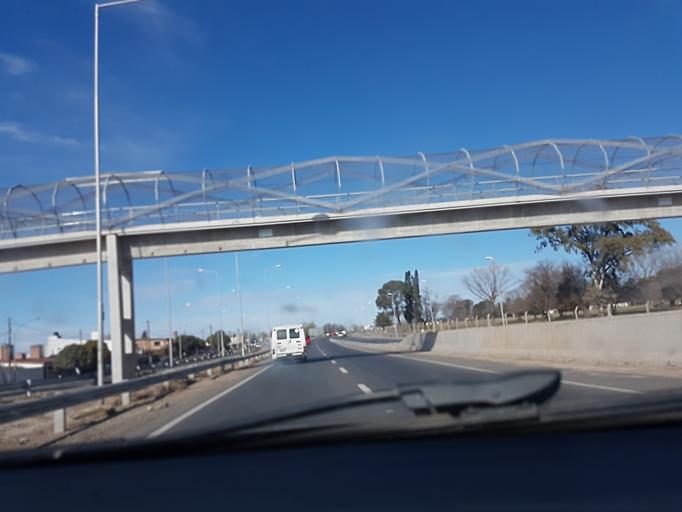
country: AR
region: Cordoba
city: La Calera
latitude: -31.3967
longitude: -64.2674
